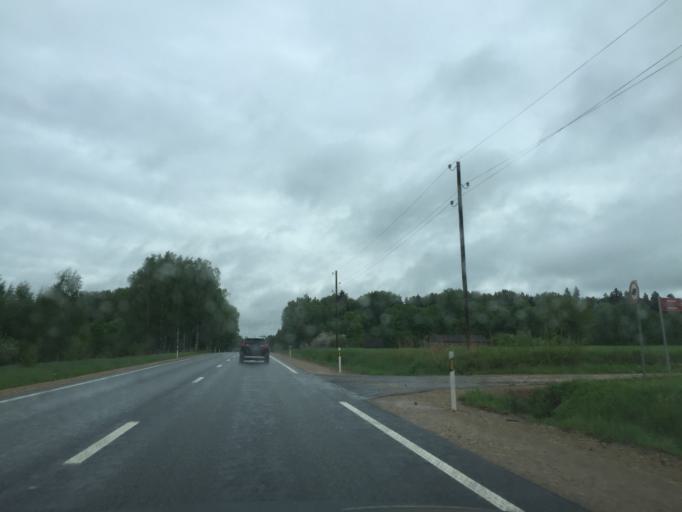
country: LV
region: Ogre
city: Jumprava
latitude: 56.6776
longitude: 24.8975
